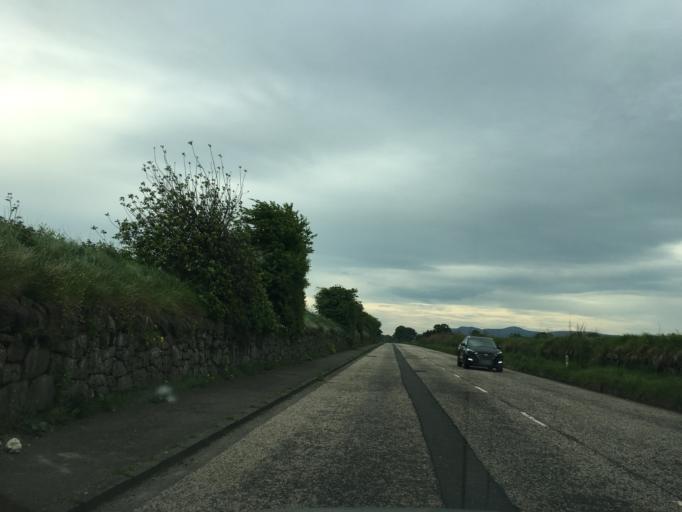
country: GB
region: Scotland
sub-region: Edinburgh
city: Ratho
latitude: 55.9483
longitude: -3.3309
